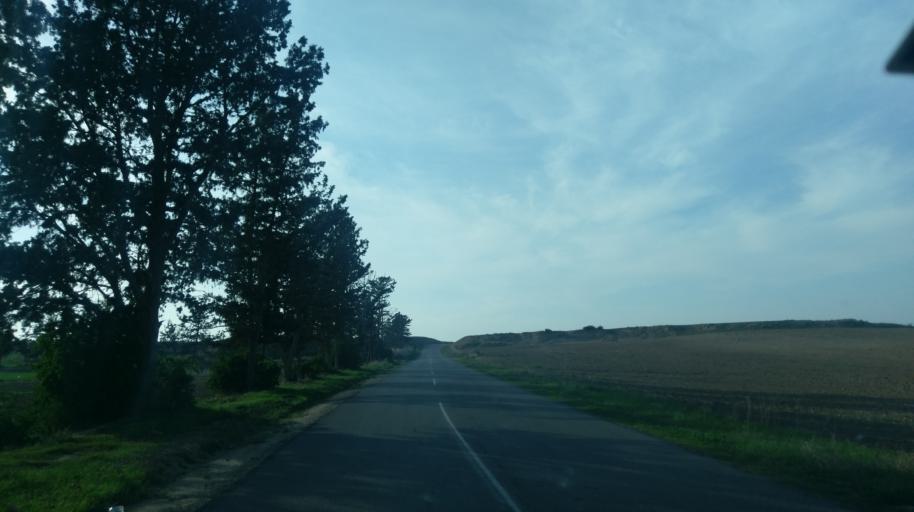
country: CY
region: Ammochostos
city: Achna
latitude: 35.1024
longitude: 33.7761
